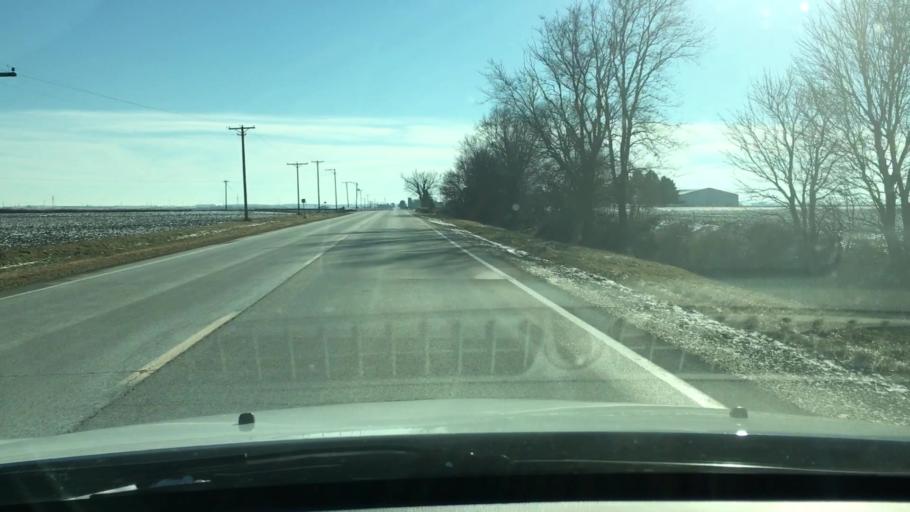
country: US
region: Illinois
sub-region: Ogle County
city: Rochelle
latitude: 41.8195
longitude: -89.0833
